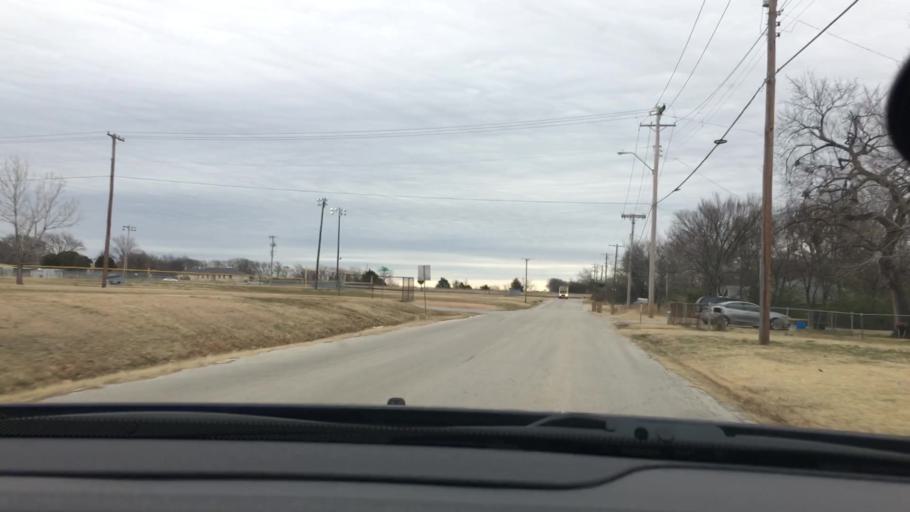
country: US
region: Oklahoma
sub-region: Carter County
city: Ardmore
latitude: 34.1692
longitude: -97.1114
